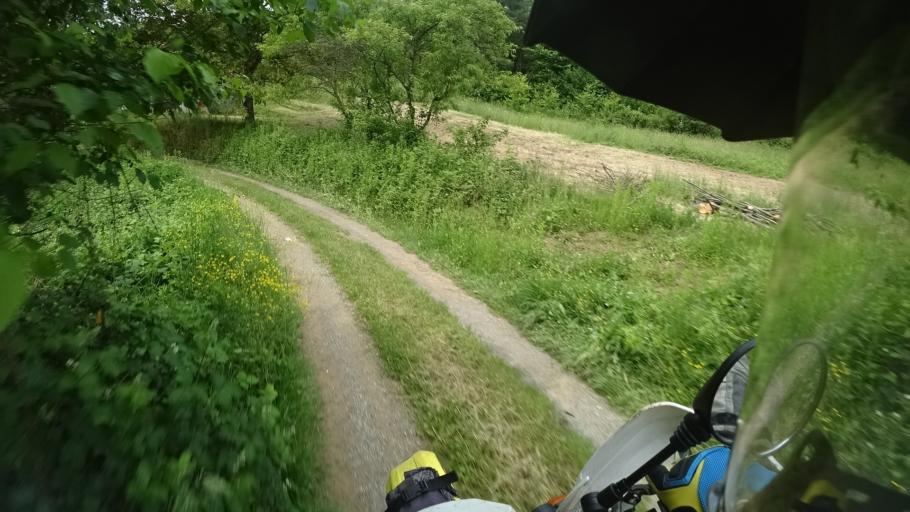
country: HR
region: Karlovacka
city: Vojnic
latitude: 45.2448
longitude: 15.6331
